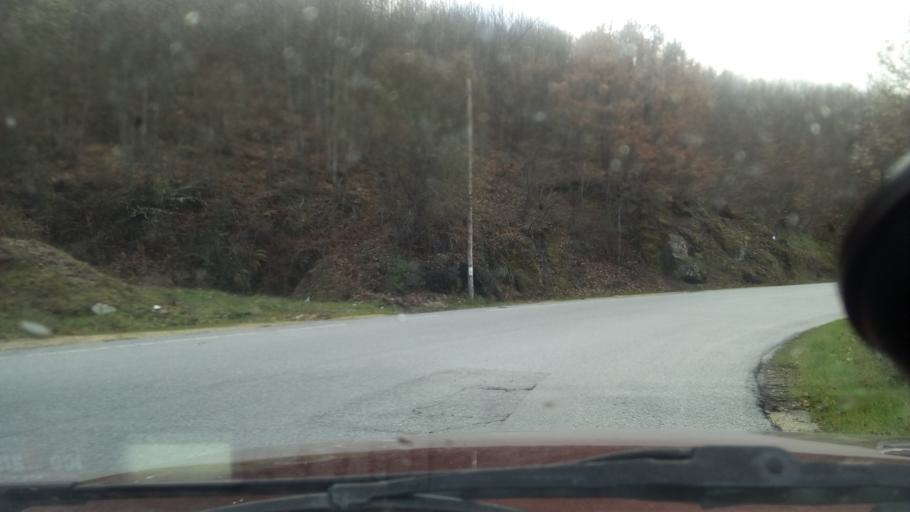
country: PT
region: Guarda
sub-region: Guarda
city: Guarda
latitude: 40.5506
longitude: -7.3118
